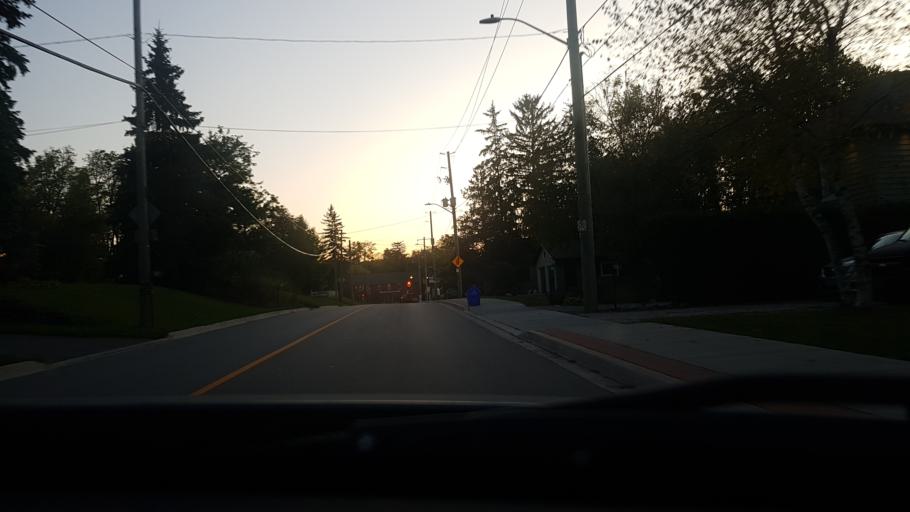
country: CA
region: Ontario
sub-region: Halton
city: Milton
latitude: 43.4885
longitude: -79.9805
